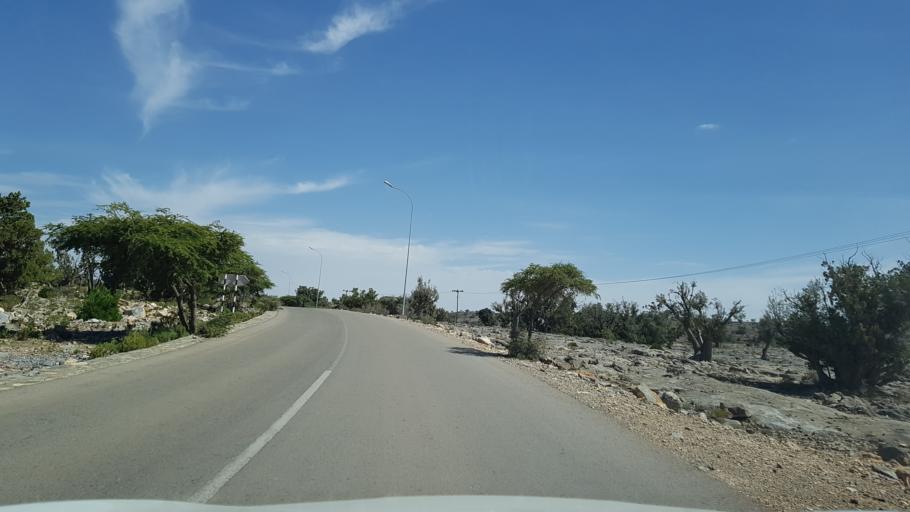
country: OM
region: Al Batinah
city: Bayt al `Awabi
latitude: 23.1315
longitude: 57.5961
